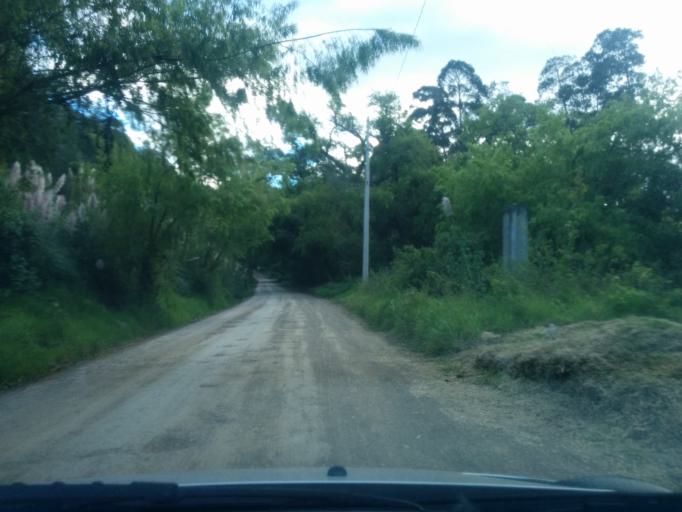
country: EC
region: Azuay
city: Cuenca
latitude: -2.8891
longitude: -78.9560
